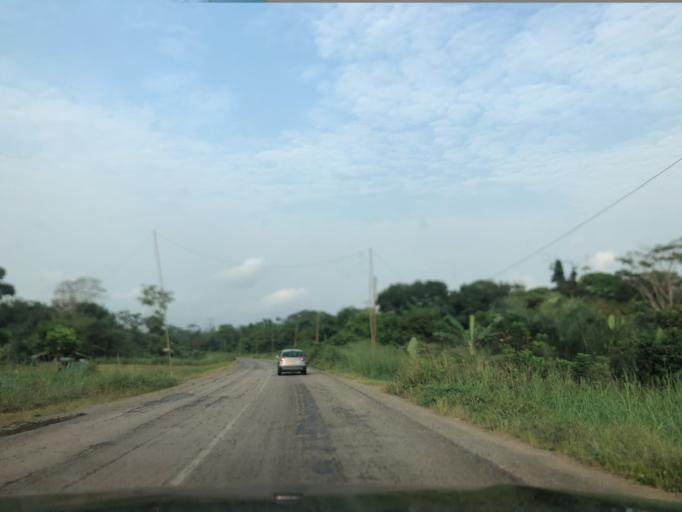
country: CM
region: Littoral
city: Dizangue
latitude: 3.4101
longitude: 10.1216
